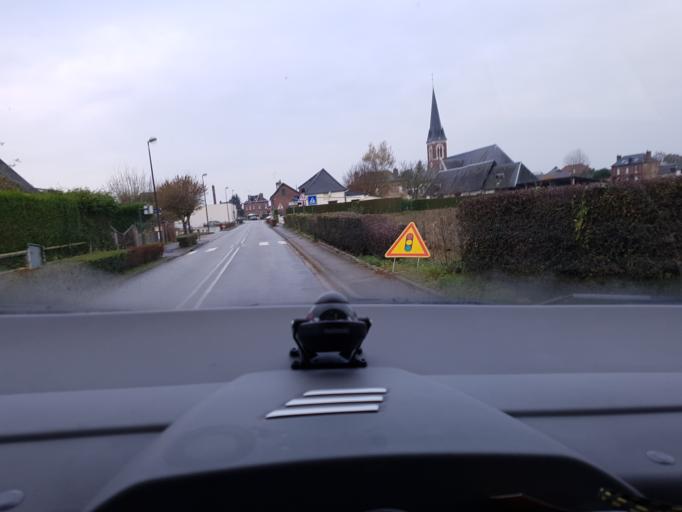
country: FR
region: Haute-Normandie
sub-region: Departement de la Seine-Maritime
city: Saint-Pierre-de-Varengeville
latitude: 49.5012
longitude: 0.9339
